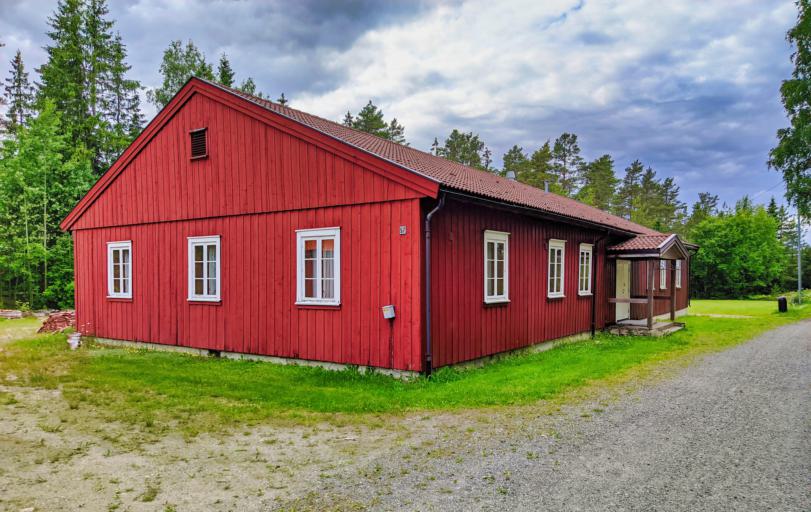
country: NO
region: Ostfold
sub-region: Eidsberg
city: Mysen
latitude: 59.5647
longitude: 11.3395
